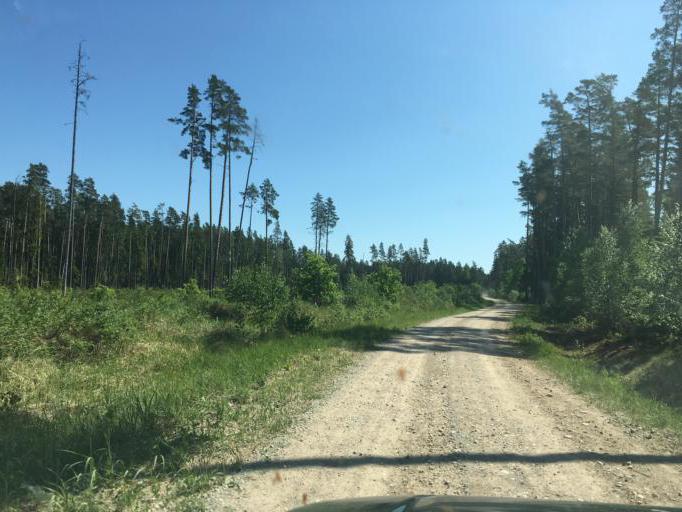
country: LV
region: Talsu Rajons
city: Valdemarpils
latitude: 57.4383
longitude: 22.6777
